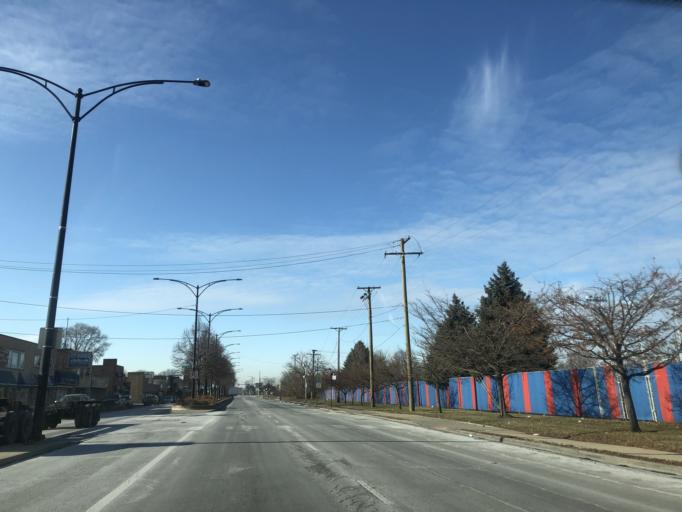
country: US
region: Illinois
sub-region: Cook County
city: Evergreen Park
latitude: 41.7501
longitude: -87.6861
